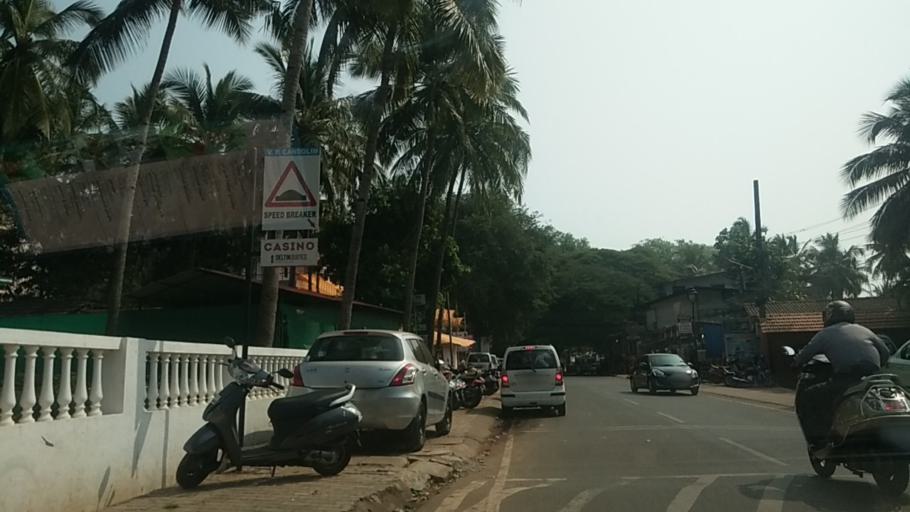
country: IN
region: Goa
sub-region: North Goa
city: Candolim
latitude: 15.5147
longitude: 73.7685
